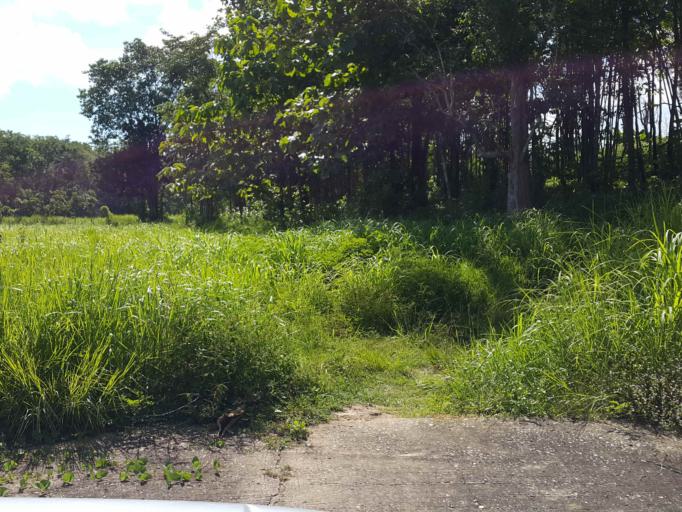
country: TH
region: Chiang Mai
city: Mae Taeng
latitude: 18.9694
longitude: 98.9095
